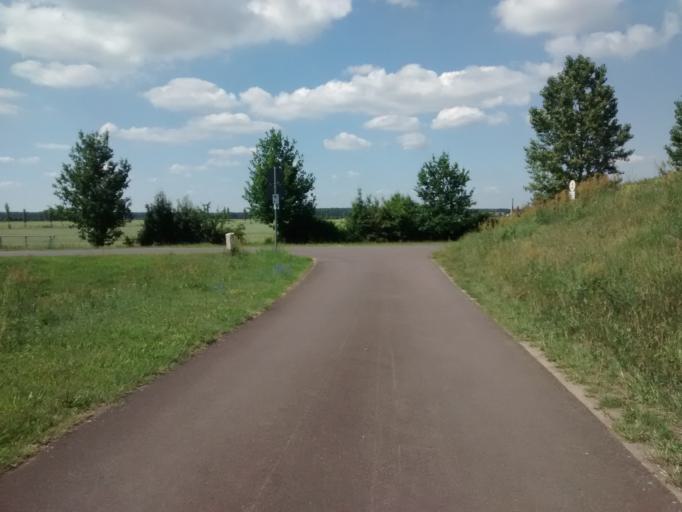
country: DE
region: Saxony-Anhalt
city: Wittenburg
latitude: 51.8458
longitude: 12.6123
